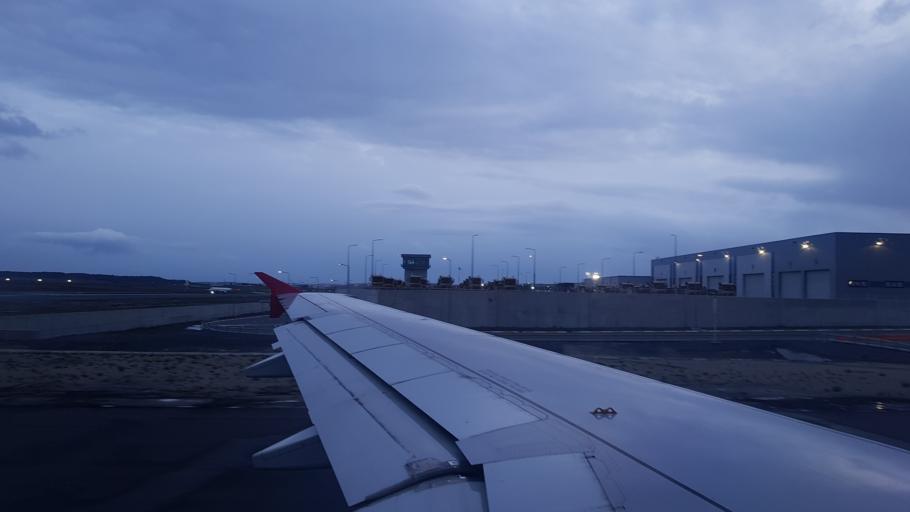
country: TR
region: Istanbul
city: Durusu
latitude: 41.2651
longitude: 28.7198
